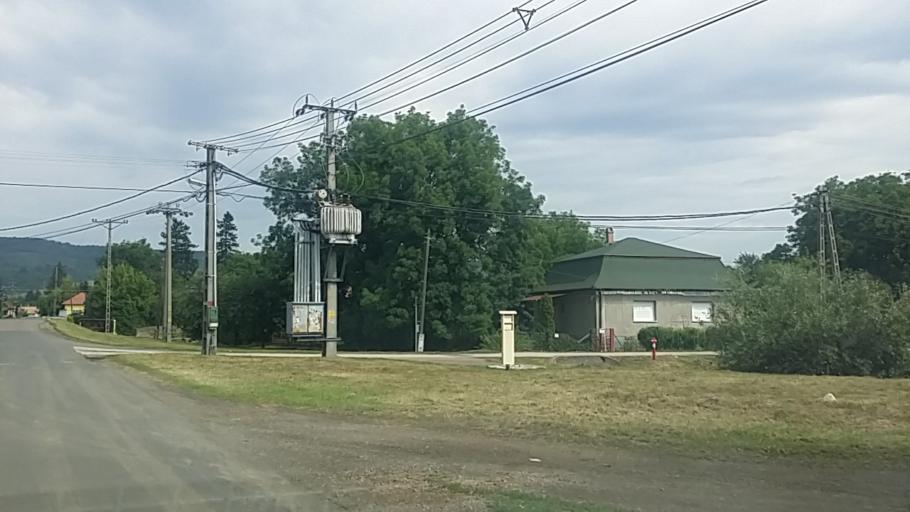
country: HU
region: Nograd
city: Matraverebely
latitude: 47.9708
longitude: 19.7805
